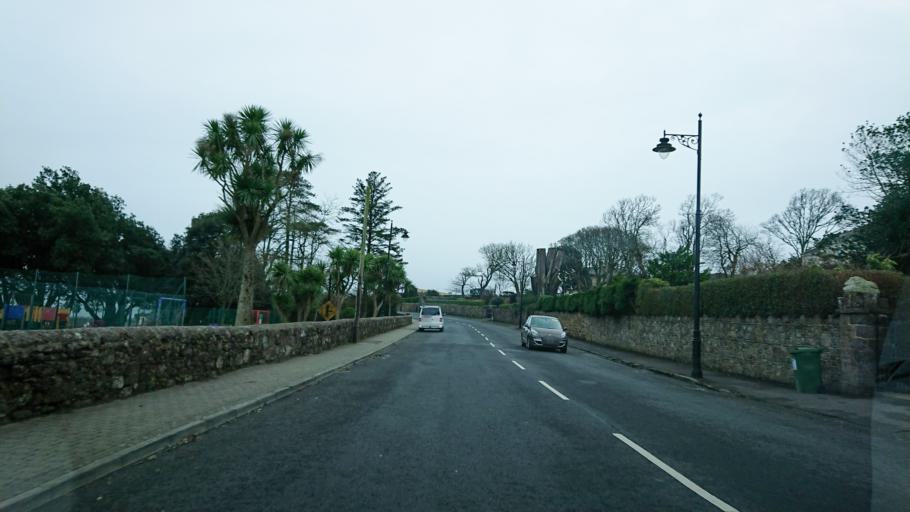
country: IE
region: Munster
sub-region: Waterford
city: Dunmore East
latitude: 52.1514
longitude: -6.9945
